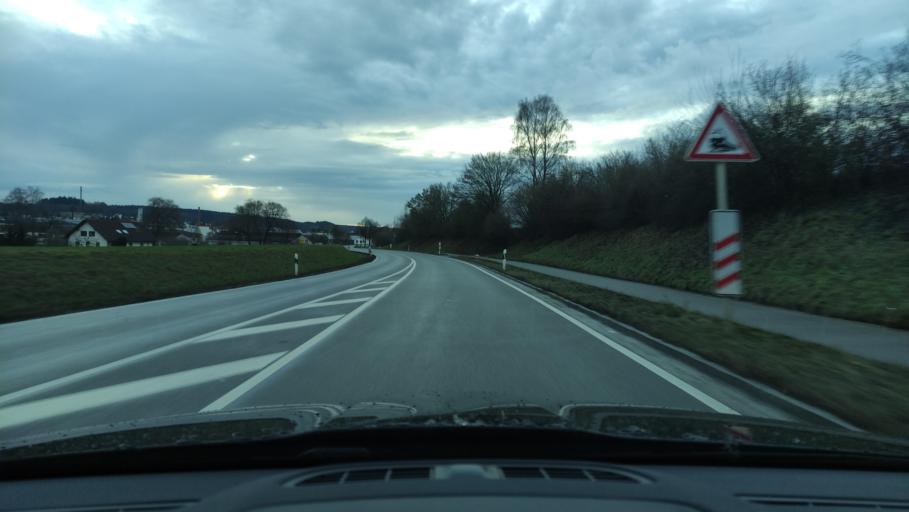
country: DE
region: Bavaria
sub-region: Swabia
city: Krumbach
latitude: 48.2570
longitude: 10.3528
